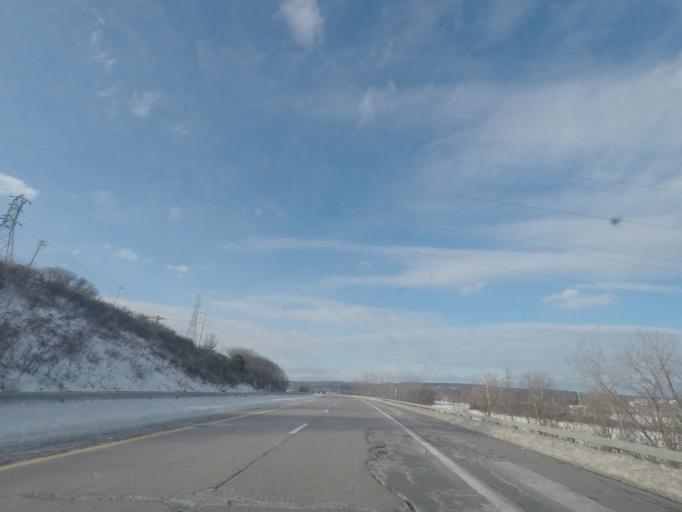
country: US
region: New York
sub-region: Schenectady County
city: Scotia
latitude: 42.8301
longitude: -73.9935
